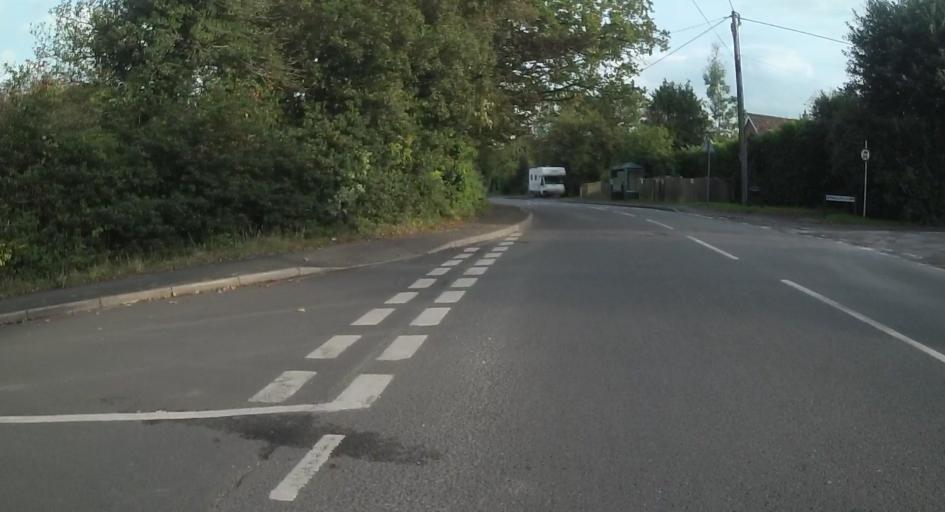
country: GB
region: England
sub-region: West Berkshire
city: Thatcham
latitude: 51.4144
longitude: -1.2246
